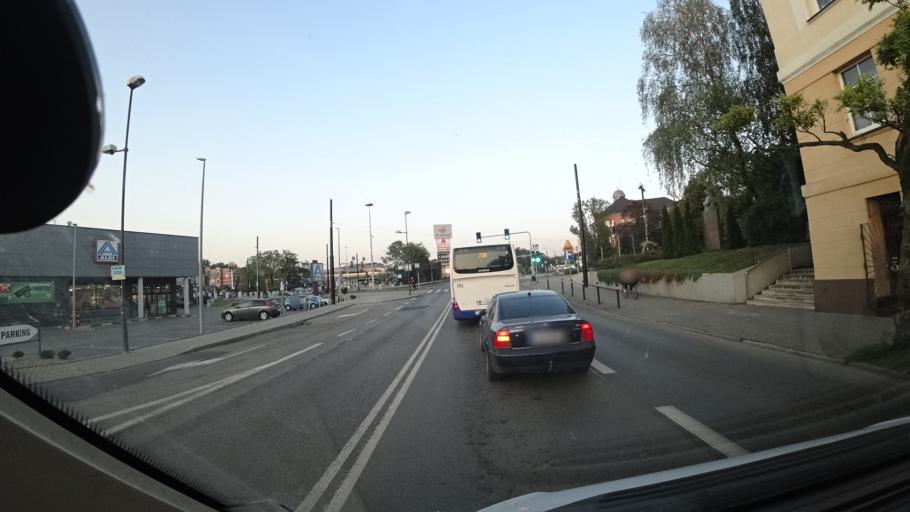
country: PL
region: Silesian Voivodeship
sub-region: Zabrze
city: Zabrze
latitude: 50.3089
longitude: 18.7850
